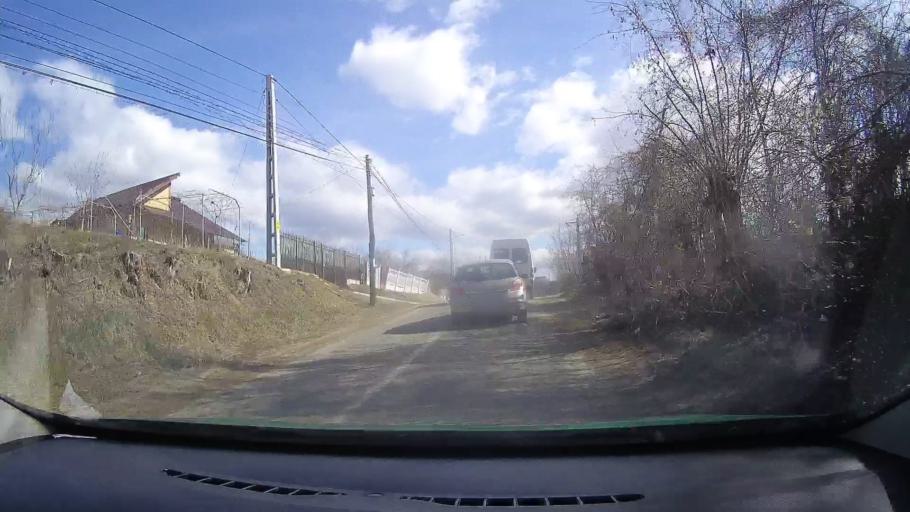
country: RO
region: Dambovita
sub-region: Comuna Glodeni
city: Laculete
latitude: 45.0212
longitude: 25.4437
